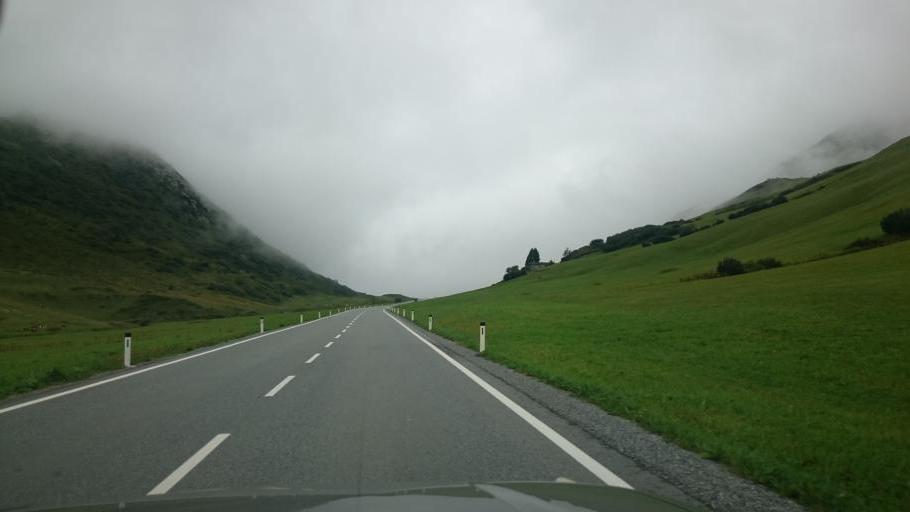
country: AT
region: Vorarlberg
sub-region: Politischer Bezirk Bludenz
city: Lech
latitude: 47.1637
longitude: 10.1642
